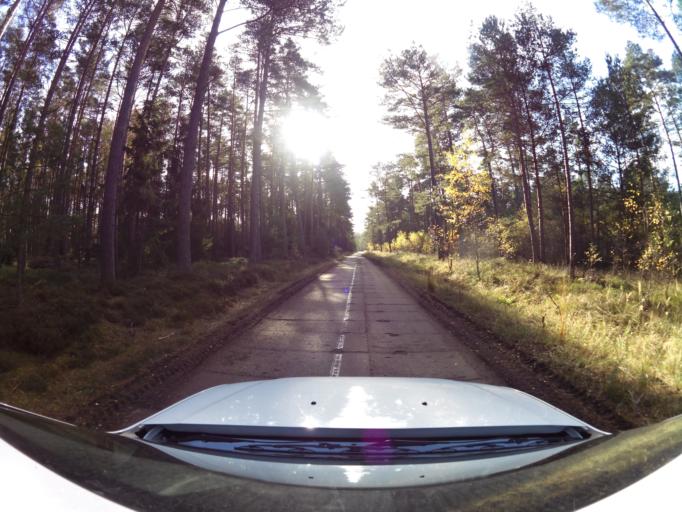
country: PL
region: West Pomeranian Voivodeship
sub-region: Powiat gryficki
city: Cerkwica
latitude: 54.1081
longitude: 15.1484
